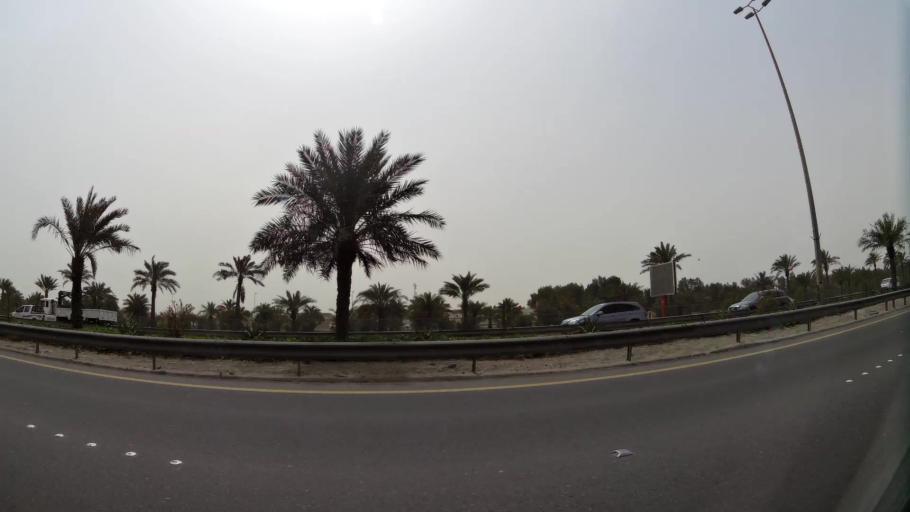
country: BH
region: Manama
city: Jidd Hafs
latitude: 26.1977
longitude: 50.5501
